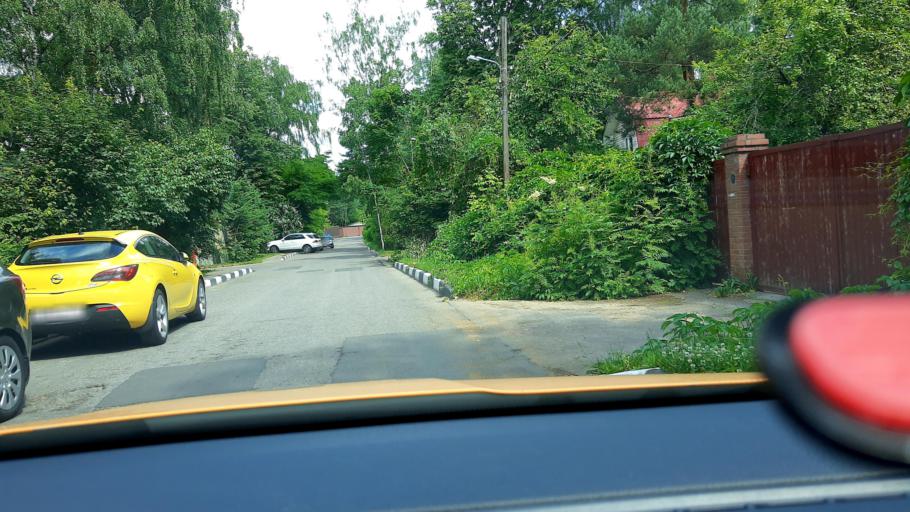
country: RU
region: Moskovskaya
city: Barvikha
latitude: 55.7409
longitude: 37.2499
